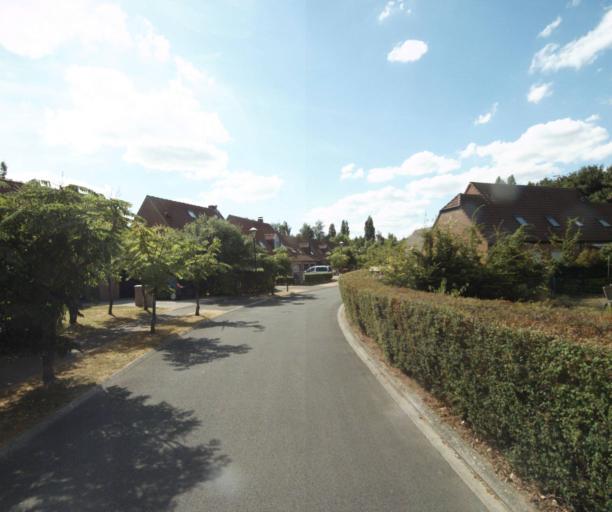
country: FR
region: Nord-Pas-de-Calais
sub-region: Departement du Nord
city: Bondues
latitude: 50.6837
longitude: 3.0934
